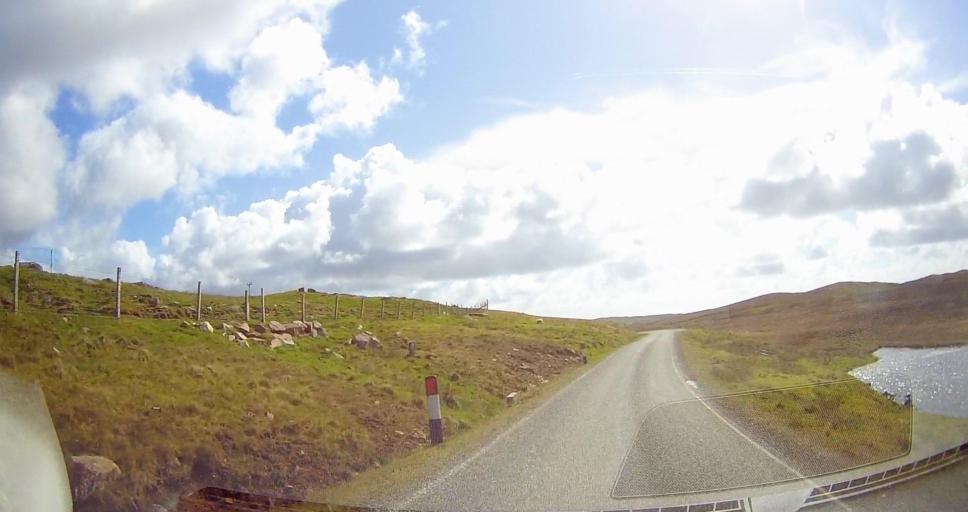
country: GB
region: Scotland
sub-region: Shetland Islands
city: Lerwick
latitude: 60.4837
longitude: -1.4033
